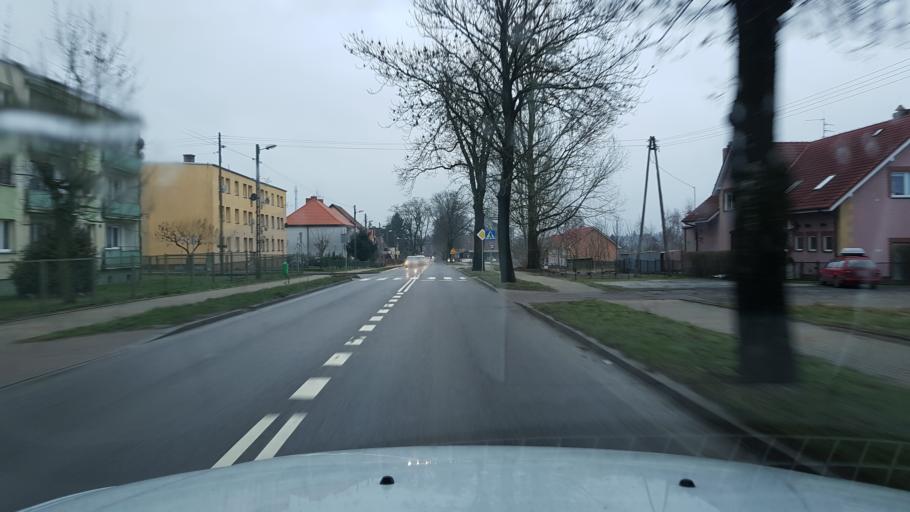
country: PL
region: West Pomeranian Voivodeship
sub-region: Powiat gryficki
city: Ploty
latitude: 53.8128
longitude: 15.2587
